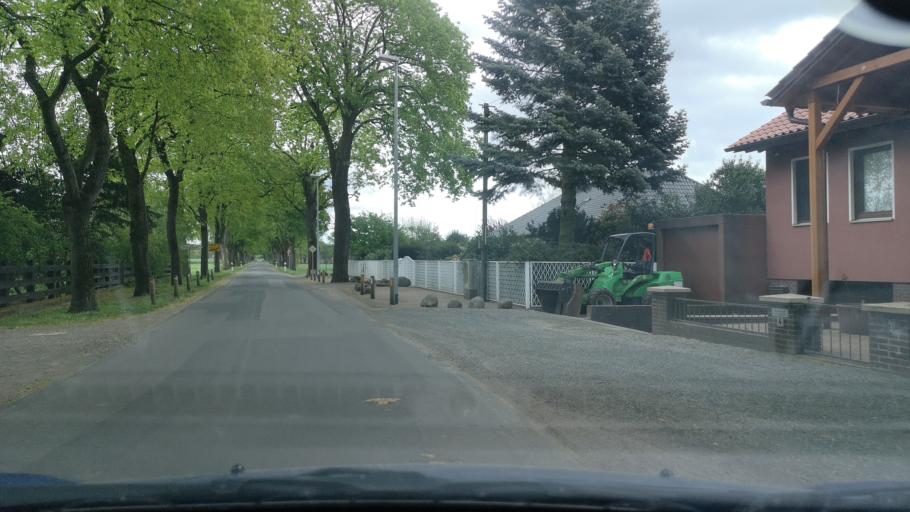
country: DE
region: Lower Saxony
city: Langenhagen
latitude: 52.4871
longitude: 9.7537
